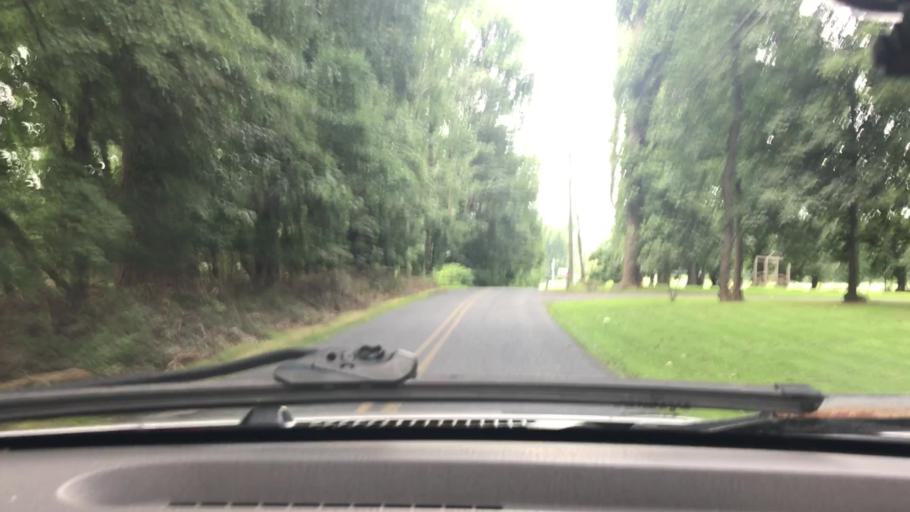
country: US
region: Pennsylvania
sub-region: Lancaster County
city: Elizabethtown
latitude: 40.1663
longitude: -76.6187
